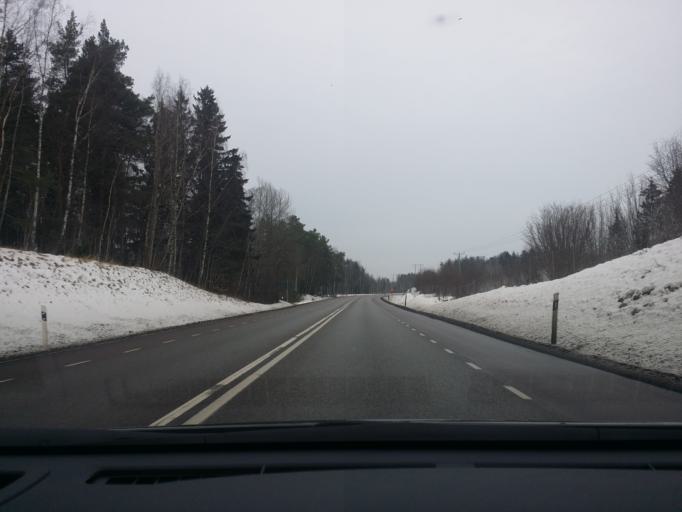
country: SE
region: Vaestra Goetaland
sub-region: Mariestads Kommun
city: Mariestad
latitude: 58.7115
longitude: 13.8762
